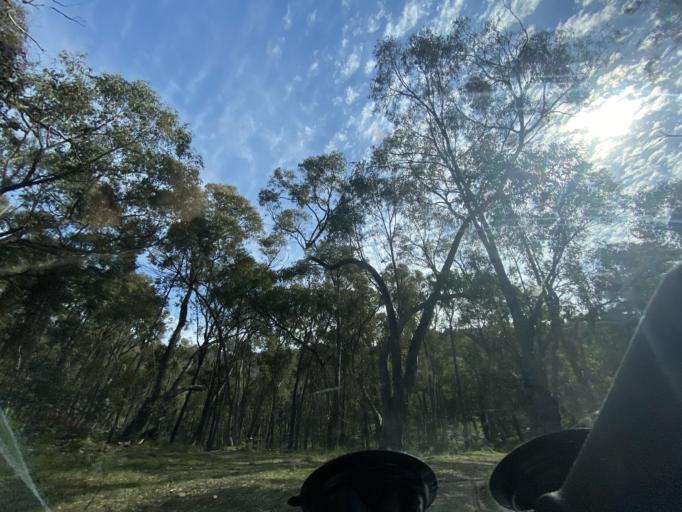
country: AU
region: Victoria
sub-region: Mansfield
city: Mansfield
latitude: -36.8087
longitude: 146.1188
